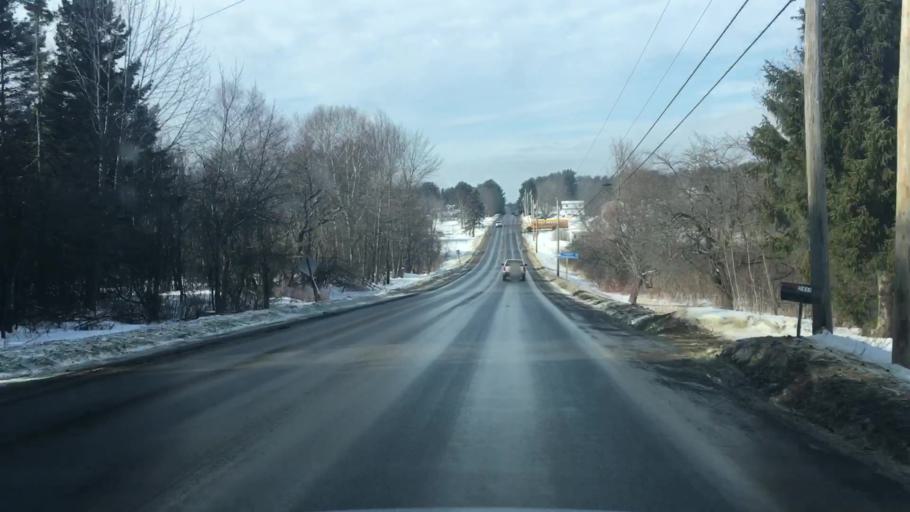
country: US
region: Maine
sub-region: Penobscot County
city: Hermon
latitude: 44.8498
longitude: -68.8780
